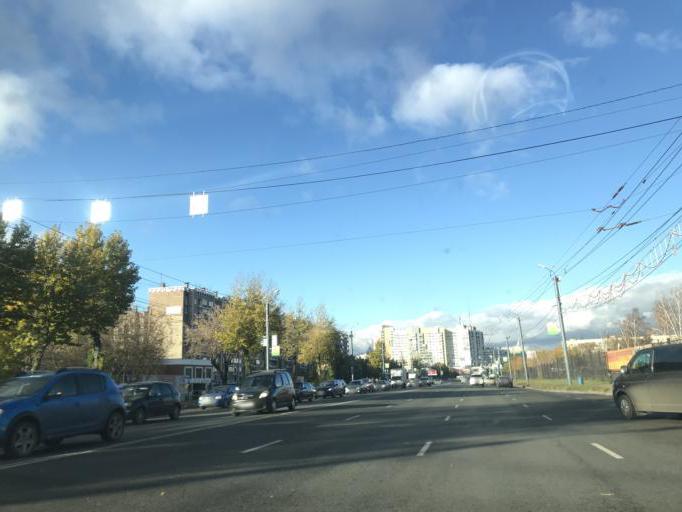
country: RU
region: Chelyabinsk
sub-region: Gorod Chelyabinsk
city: Chelyabinsk
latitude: 55.1672
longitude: 61.4527
